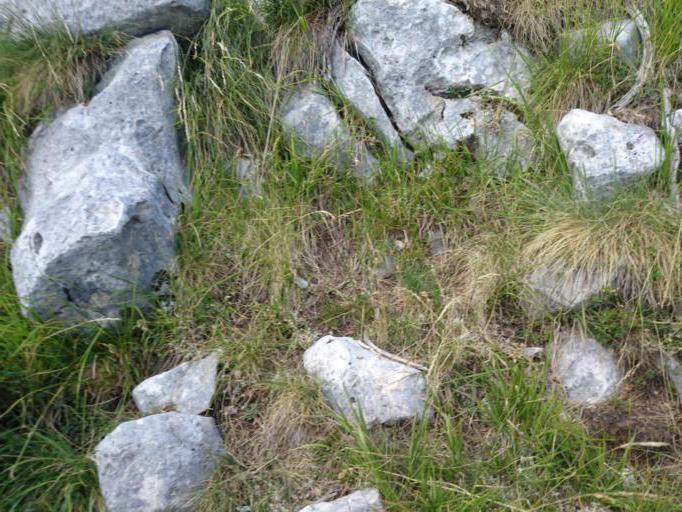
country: AL
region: Berat
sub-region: Rrethi i Beratit
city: Polican
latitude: 40.6622
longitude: 20.1592
